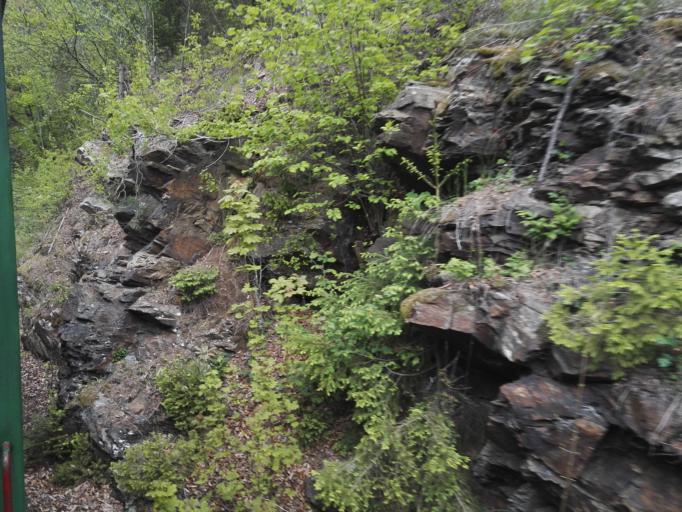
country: AT
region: Styria
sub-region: Politischer Bezirk Weiz
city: Birkfeld
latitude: 47.3424
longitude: 15.7006
